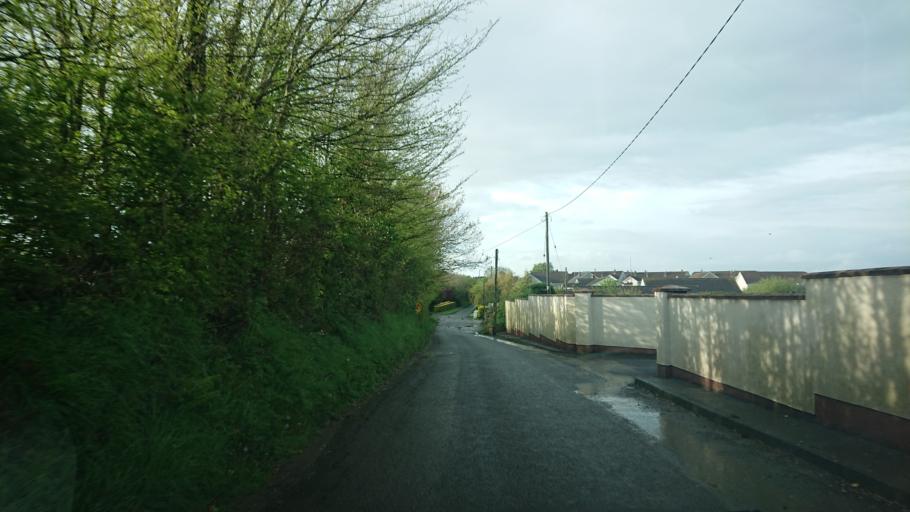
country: IE
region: Munster
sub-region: Waterford
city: Waterford
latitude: 52.2382
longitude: -7.1321
